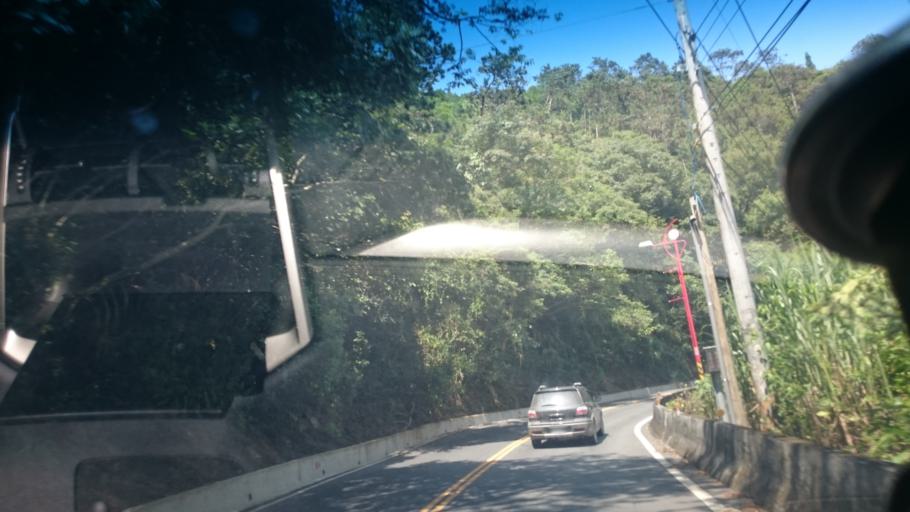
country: TW
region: Taiwan
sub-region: Nantou
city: Puli
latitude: 24.0269
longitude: 121.1393
